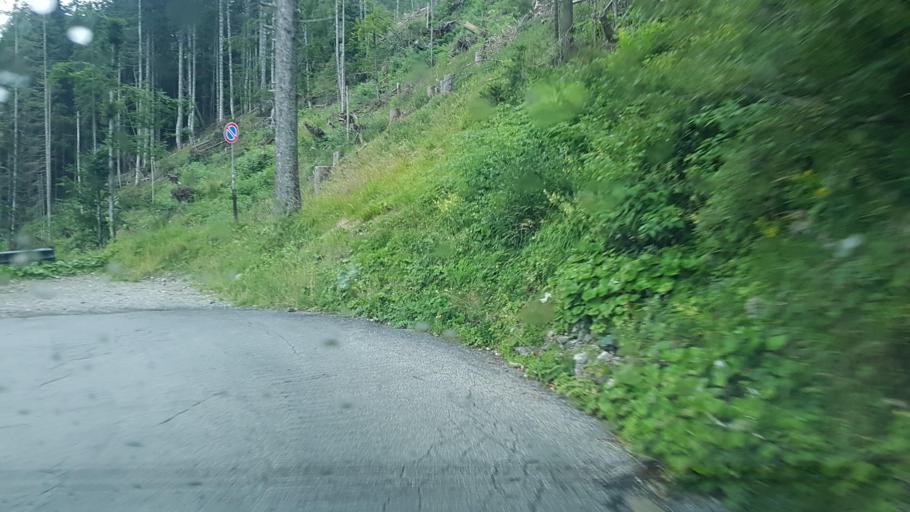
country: IT
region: Veneto
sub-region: Provincia di Belluno
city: Granvilla
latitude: 46.5821
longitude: 12.7261
